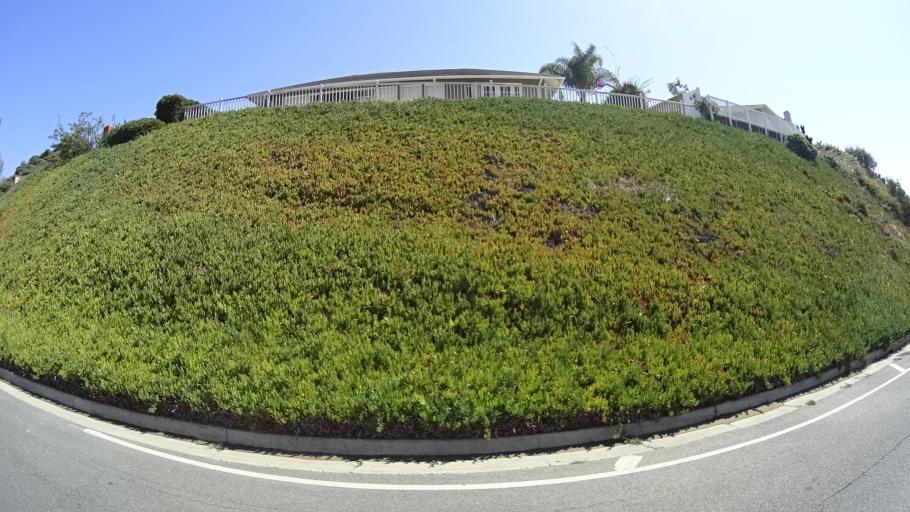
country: US
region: California
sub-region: Orange County
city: San Clemente
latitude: 33.4508
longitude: -117.6455
